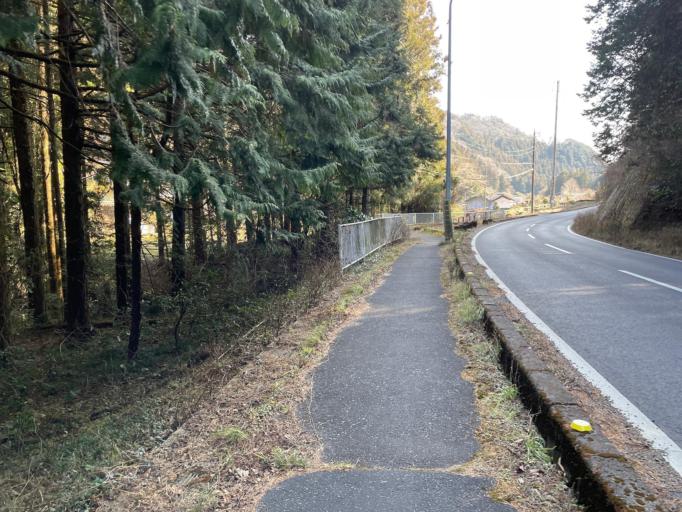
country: JP
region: Saitama
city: Hanno
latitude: 35.8524
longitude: 139.2507
